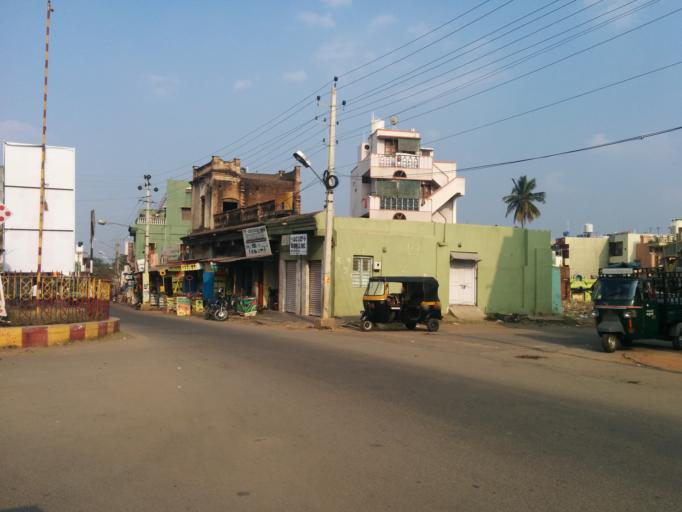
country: IN
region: Karnataka
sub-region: Mysore
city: Mysore
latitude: 12.2954
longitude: 76.6498
